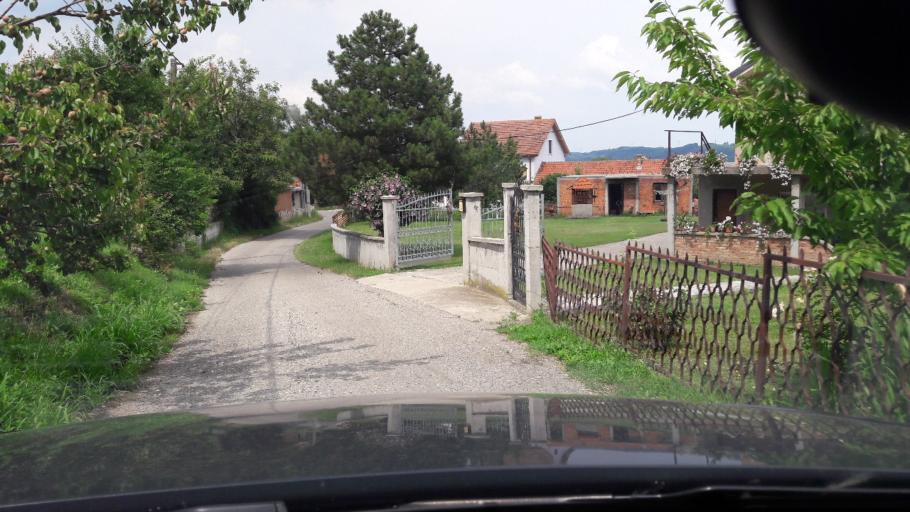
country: RS
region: Central Serbia
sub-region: Belgrade
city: Grocka
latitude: 44.6491
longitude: 20.5975
